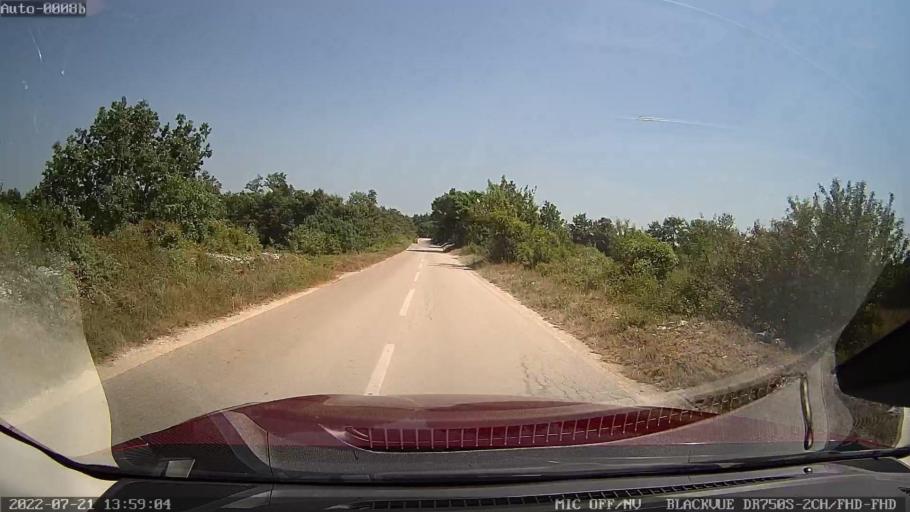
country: HR
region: Istarska
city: Vodnjan
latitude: 45.1063
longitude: 13.8585
